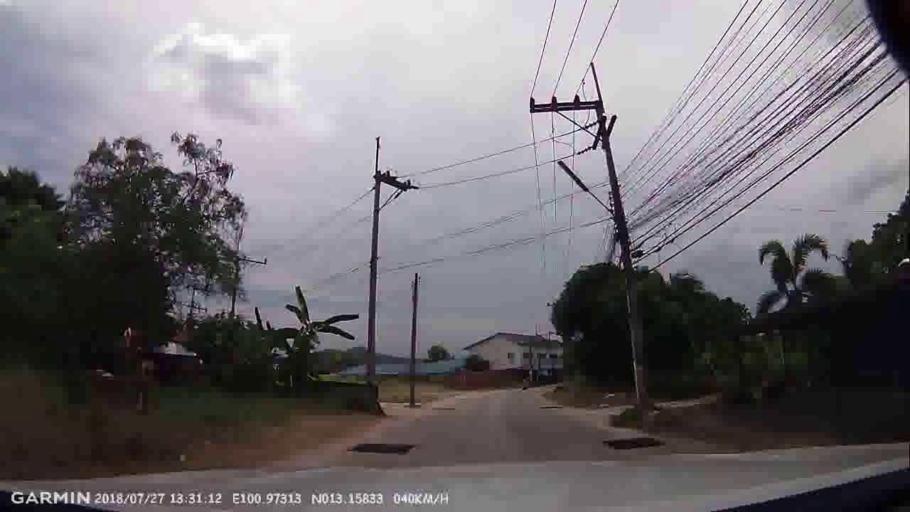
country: TH
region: Chon Buri
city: Si Racha
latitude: 13.1584
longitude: 100.9731
